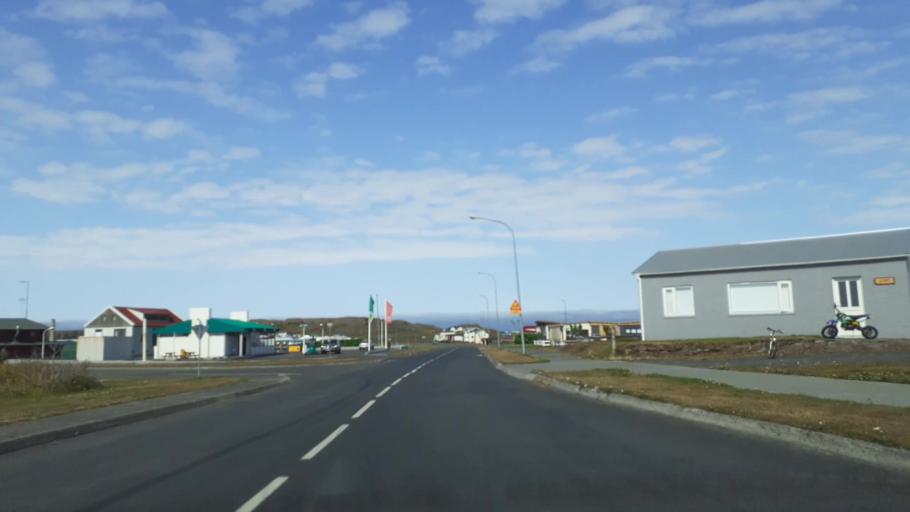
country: IS
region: Northwest
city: Saudarkrokur
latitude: 65.8231
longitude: -20.3047
